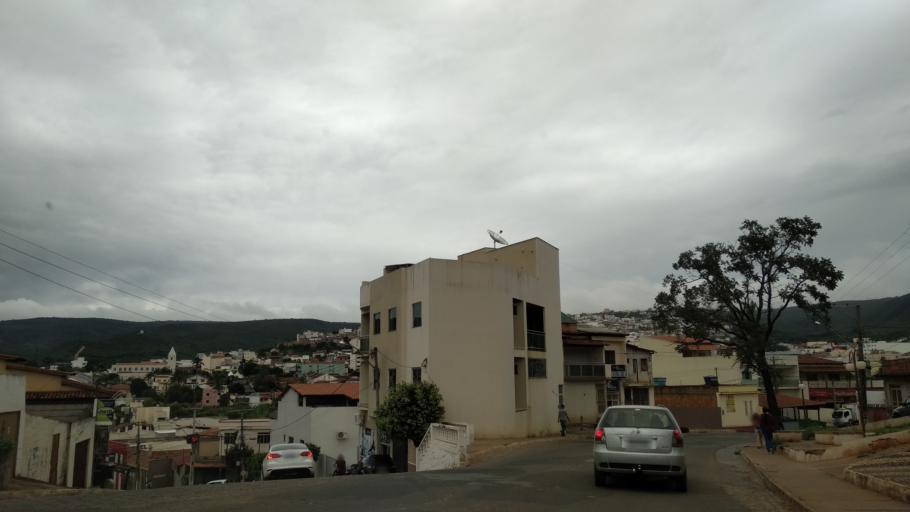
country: BR
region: Bahia
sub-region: Caetite
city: Caetite
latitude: -14.0635
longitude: -42.4847
